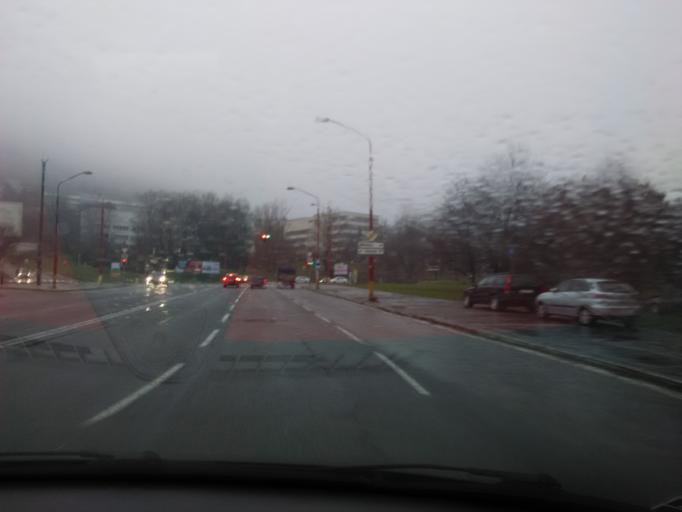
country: AT
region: Lower Austria
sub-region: Politischer Bezirk Bruck an der Leitha
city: Wolfsthal
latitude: 48.1779
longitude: 17.0474
